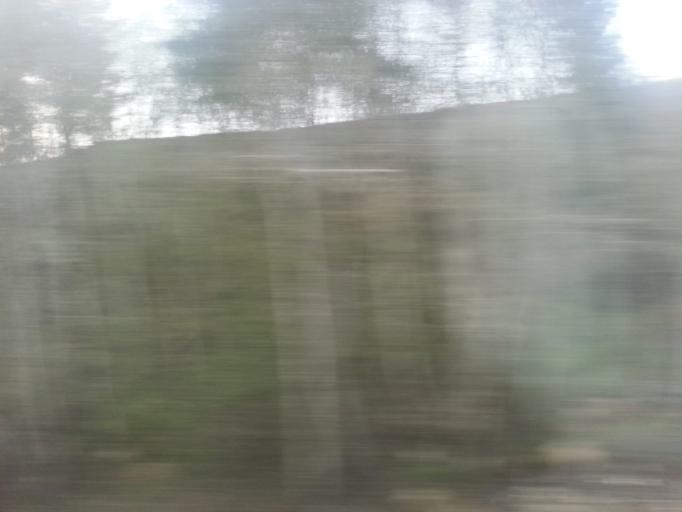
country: NO
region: Sor-Trondelag
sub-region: Melhus
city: Lundamo
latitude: 63.1643
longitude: 10.2978
